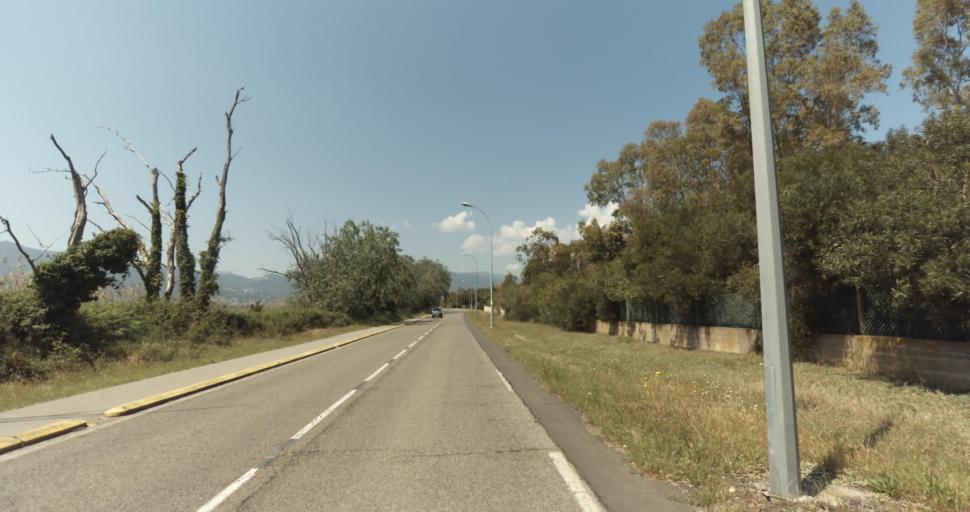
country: FR
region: Corsica
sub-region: Departement de la Haute-Corse
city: Biguglia
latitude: 42.6271
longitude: 9.4684
